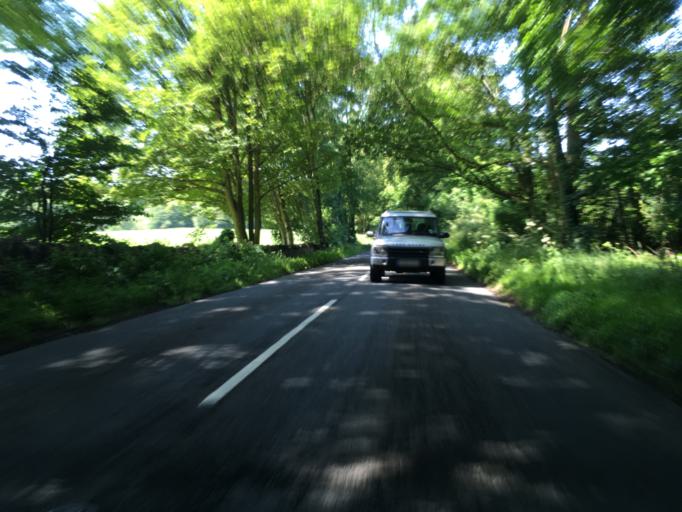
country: GB
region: England
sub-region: Gloucestershire
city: Stow on the Wold
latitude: 51.9187
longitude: -1.7752
